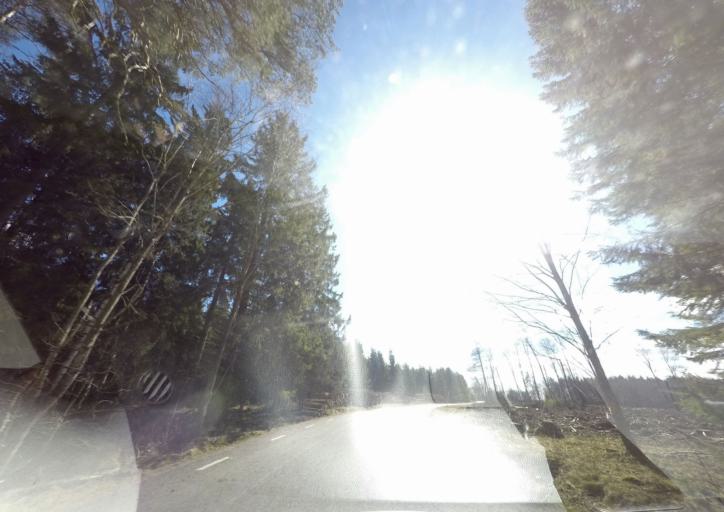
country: SE
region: OEstergoetland
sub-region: Norrkopings Kommun
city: Krokek
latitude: 58.8783
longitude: 16.3863
